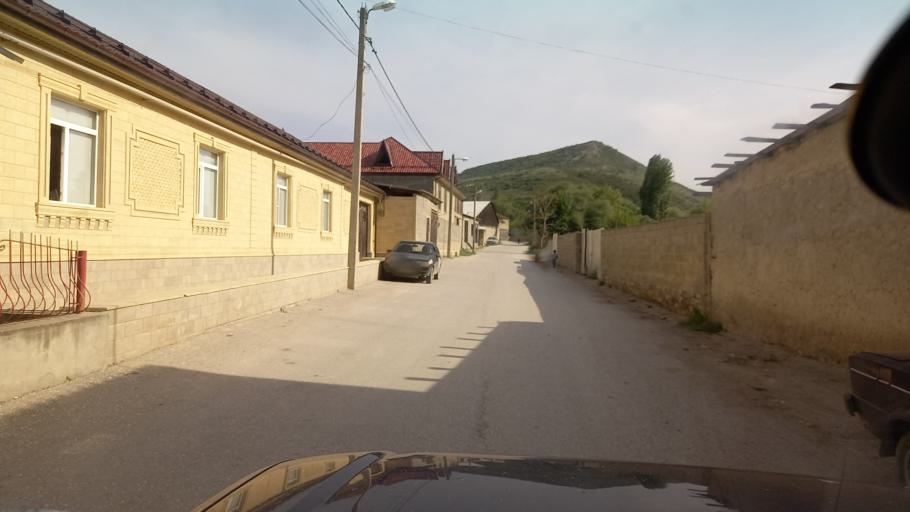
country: RU
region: Dagestan
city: Karabudakhkent
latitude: 42.7113
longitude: 47.5690
